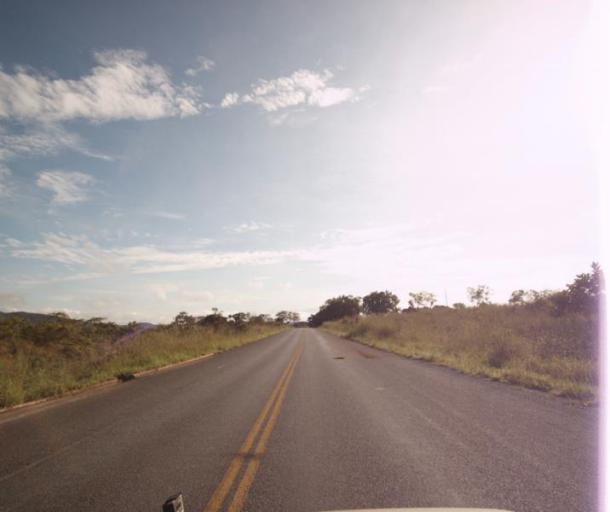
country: BR
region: Goias
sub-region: Pirenopolis
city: Pirenopolis
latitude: -15.5762
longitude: -48.6250
